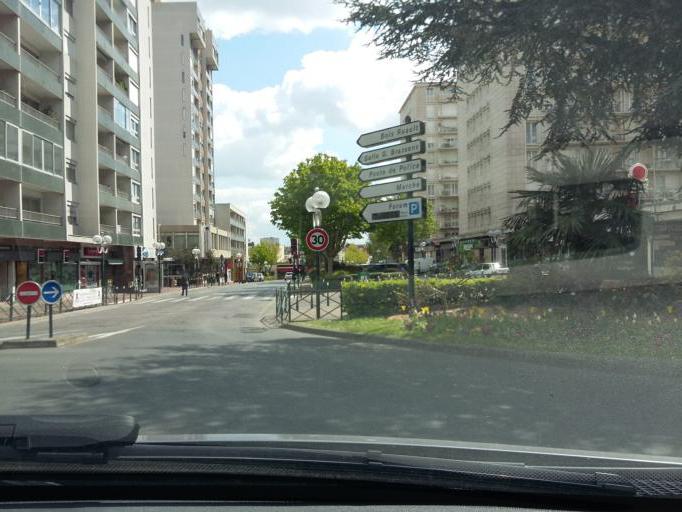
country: FR
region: Ile-de-France
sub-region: Departement du Val-d'Oise
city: Saint-Gratien
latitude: 48.9691
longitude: 2.2856
